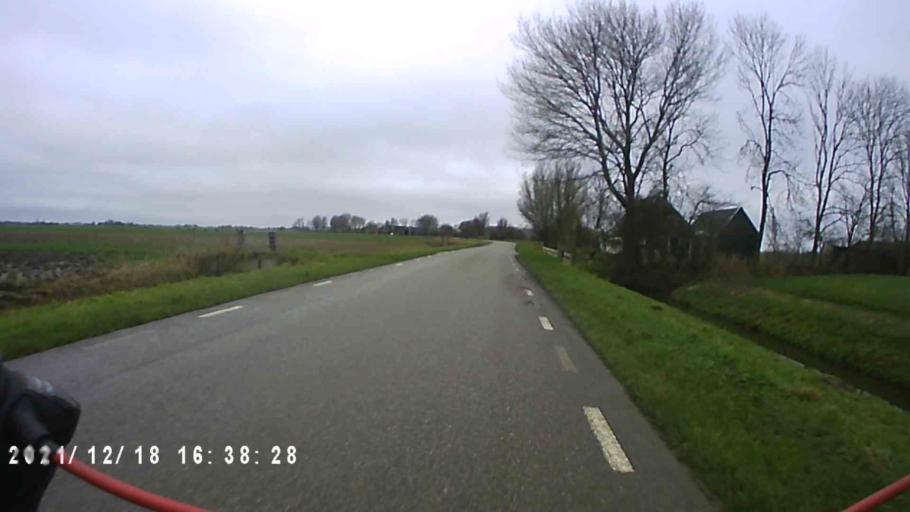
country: NL
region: Friesland
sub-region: Gemeente Dongeradeel
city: Dokkum
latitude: 53.3590
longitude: 6.0110
